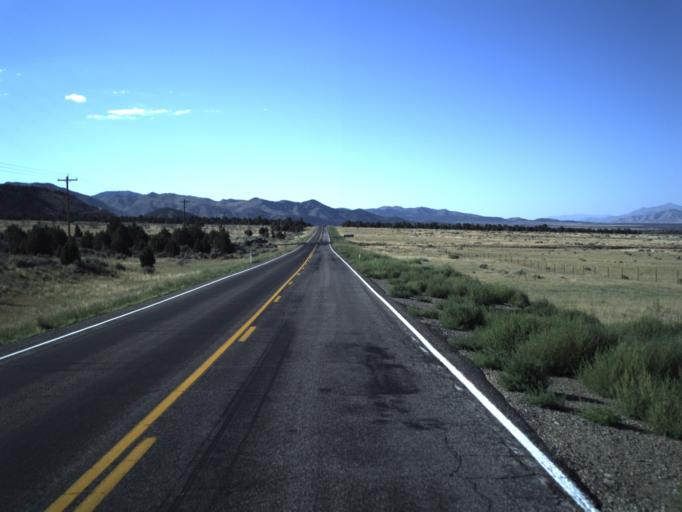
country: US
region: Utah
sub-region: Utah County
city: Genola
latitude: 39.9310
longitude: -112.1488
